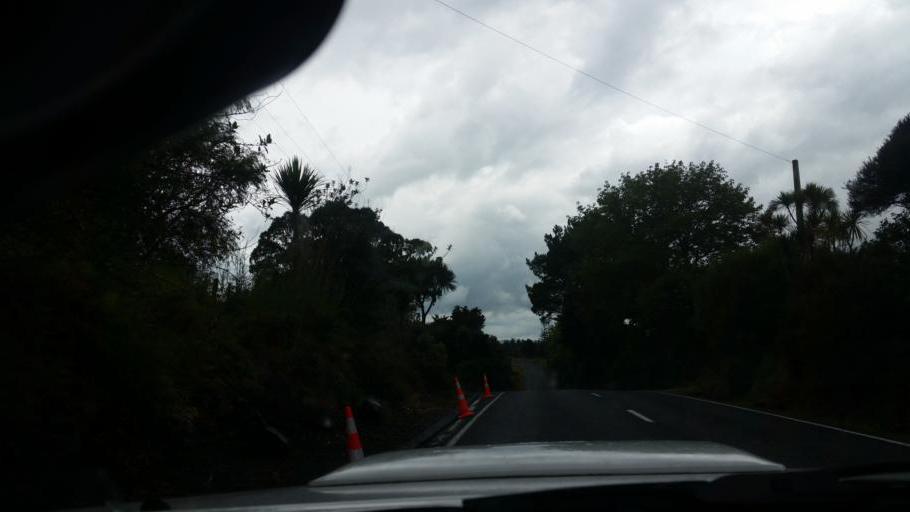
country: NZ
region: Auckland
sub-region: Auckland
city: Wellsford
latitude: -36.1484
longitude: 174.2215
